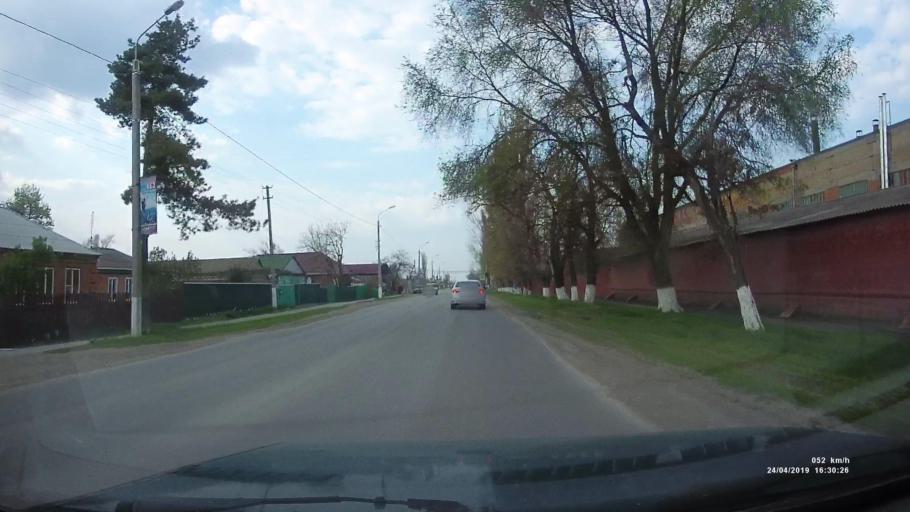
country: RU
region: Rostov
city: Orlovskiy
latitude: 46.8751
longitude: 42.0384
